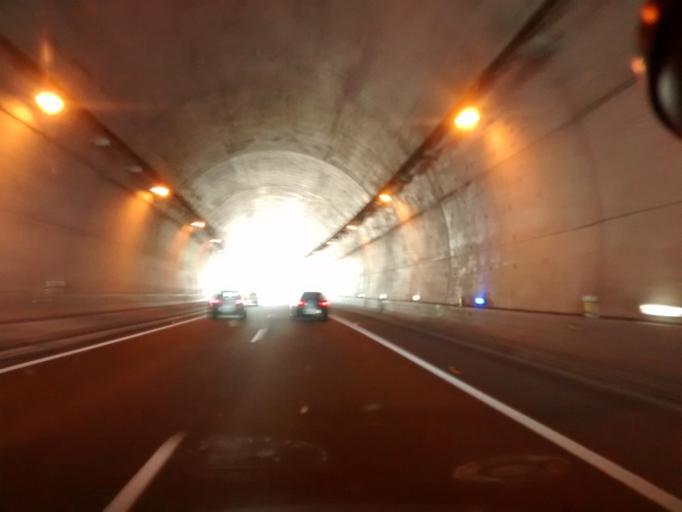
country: ES
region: Basque Country
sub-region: Provincia de Guipuzcoa
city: Hernani
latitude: 43.2769
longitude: -1.9713
